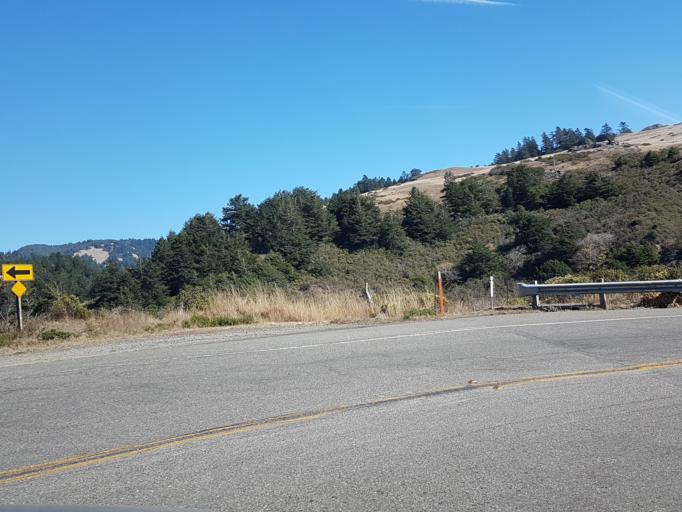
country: US
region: California
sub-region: Sonoma County
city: Monte Rio
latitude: 38.4759
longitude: -123.1541
